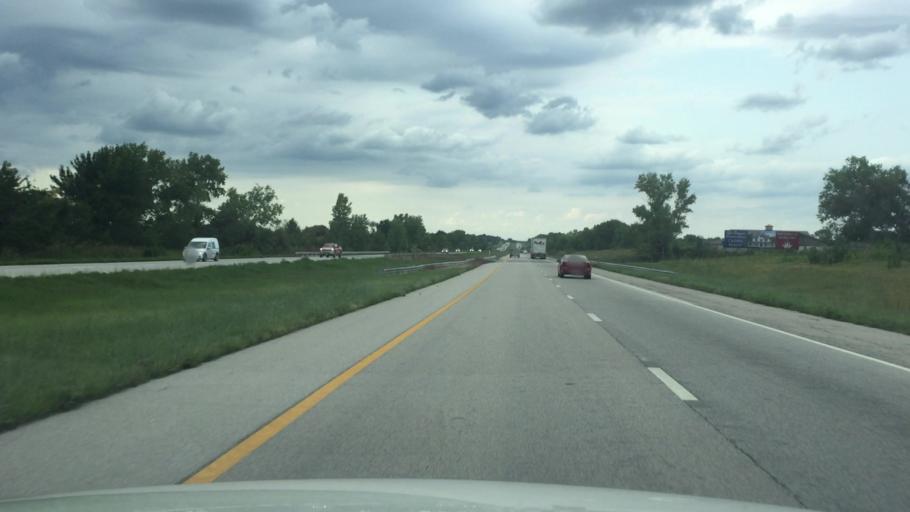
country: US
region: Kansas
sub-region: Miami County
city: Louisburg
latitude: 38.7515
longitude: -94.6774
